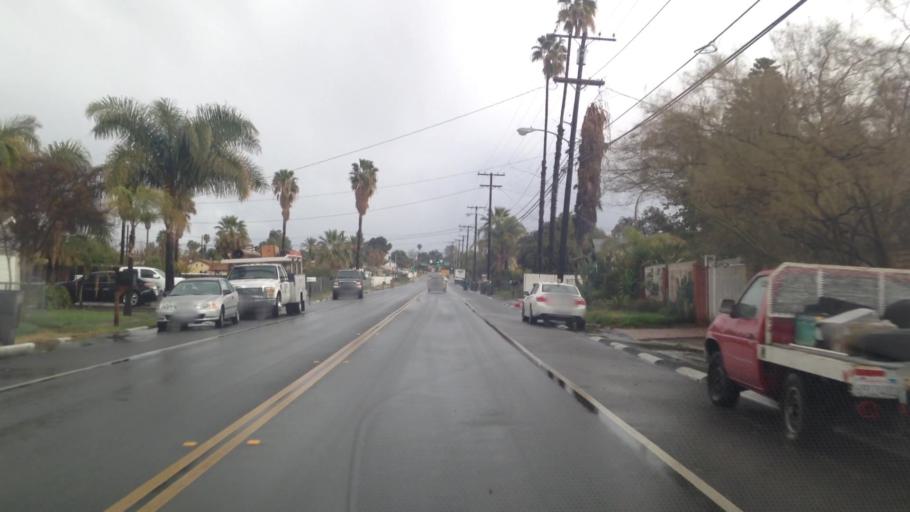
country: US
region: California
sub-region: Riverside County
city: Pedley
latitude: 33.9259
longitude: -117.4767
